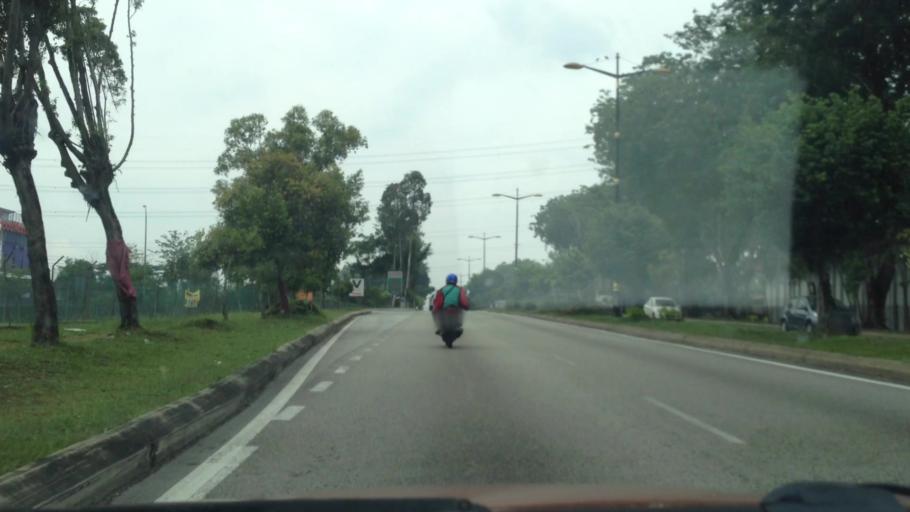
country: MY
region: Selangor
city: Shah Alam
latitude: 3.0632
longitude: 101.5411
